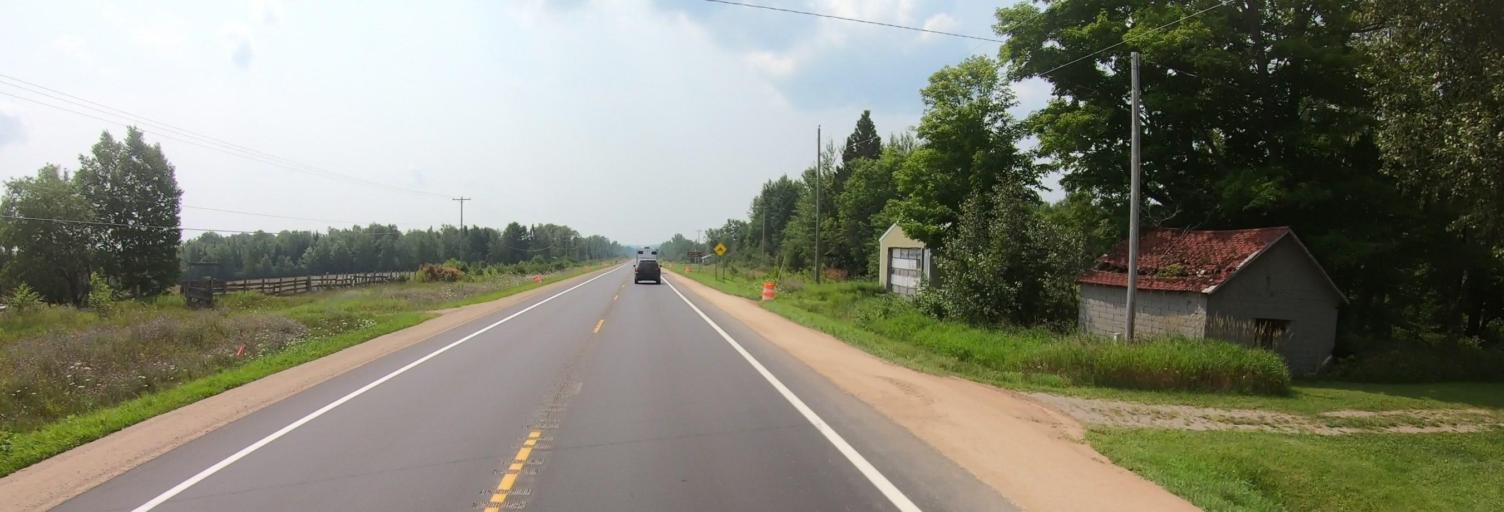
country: US
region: Michigan
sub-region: Luce County
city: Newberry
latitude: 46.3995
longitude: -85.5099
